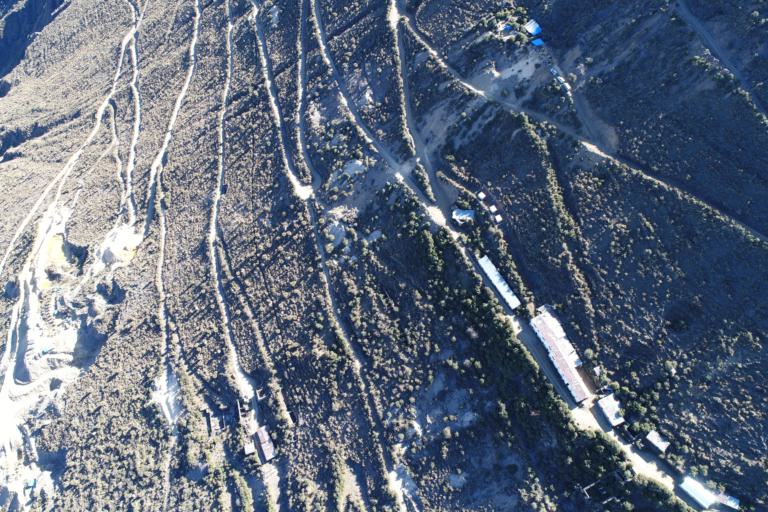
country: BO
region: La Paz
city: Viloco
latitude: -16.8188
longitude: -67.5511
